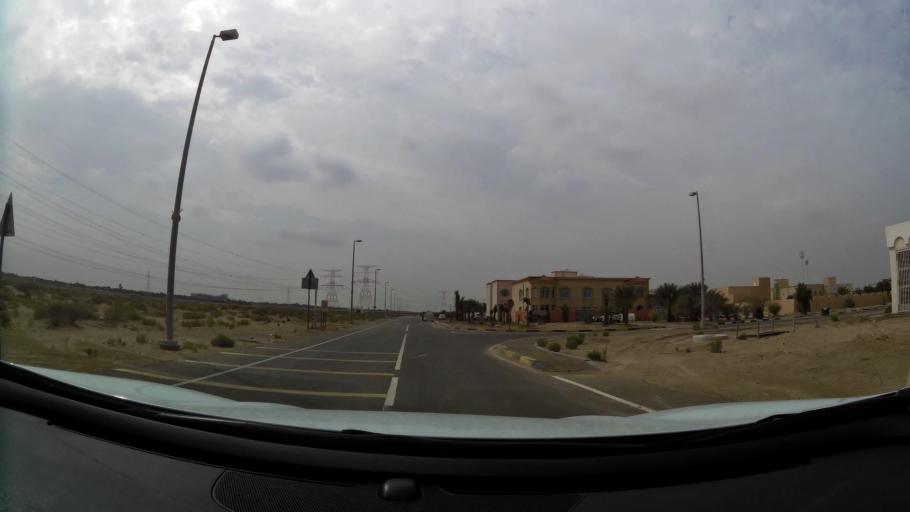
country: AE
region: Abu Dhabi
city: Abu Dhabi
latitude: 24.6341
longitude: 54.6928
